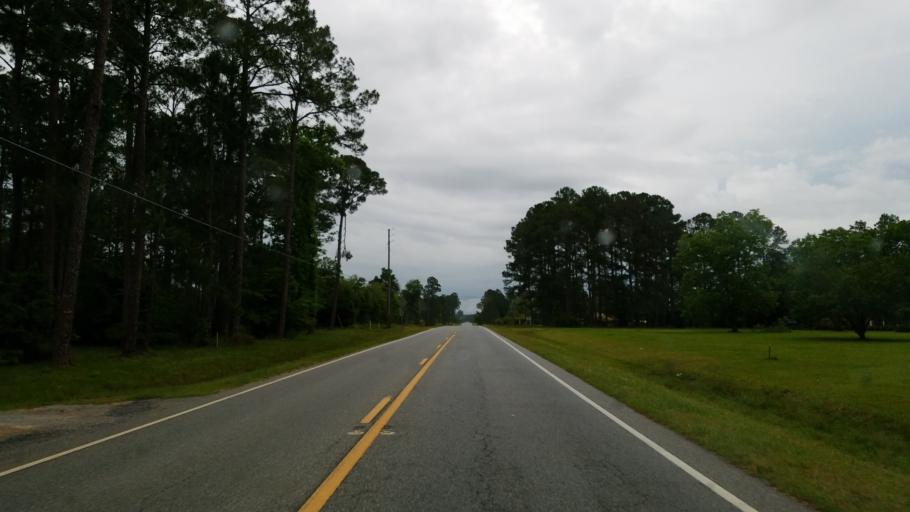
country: US
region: Georgia
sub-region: Berrien County
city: Ray City
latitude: 31.0626
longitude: -83.1608
